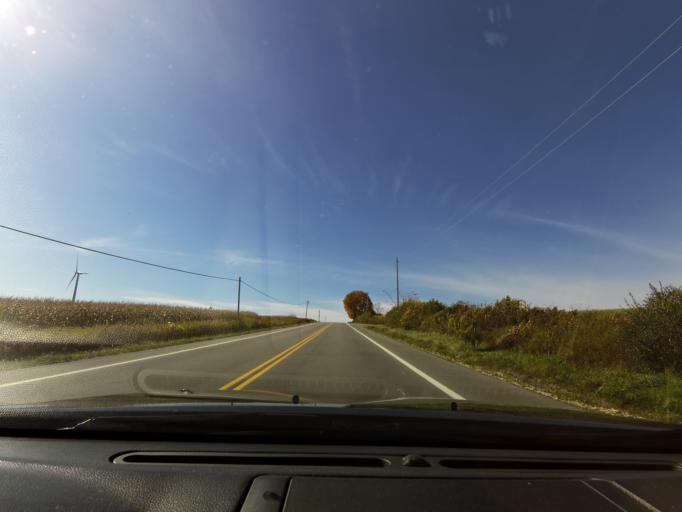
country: US
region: New York
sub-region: Wyoming County
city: Warsaw
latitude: 42.6380
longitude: -78.2310
